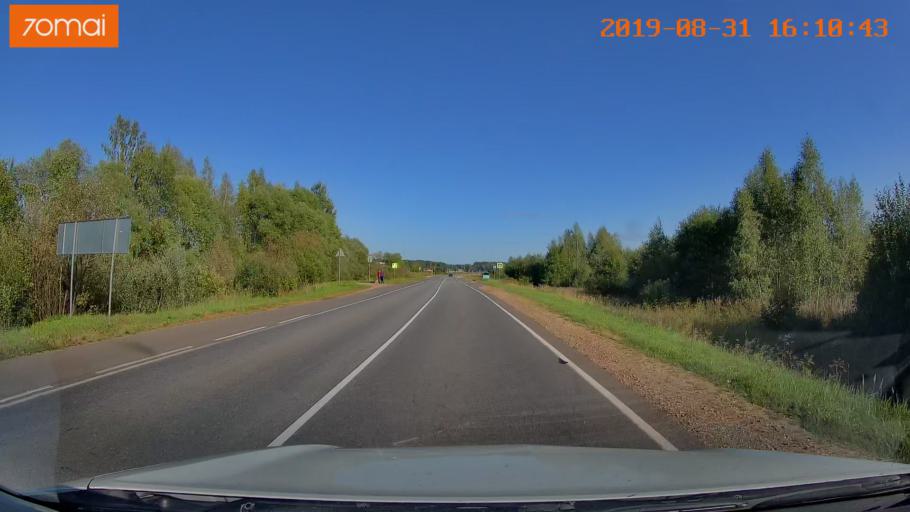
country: RU
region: Kaluga
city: Nikola-Lenivets
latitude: 54.5826
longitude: 35.4308
